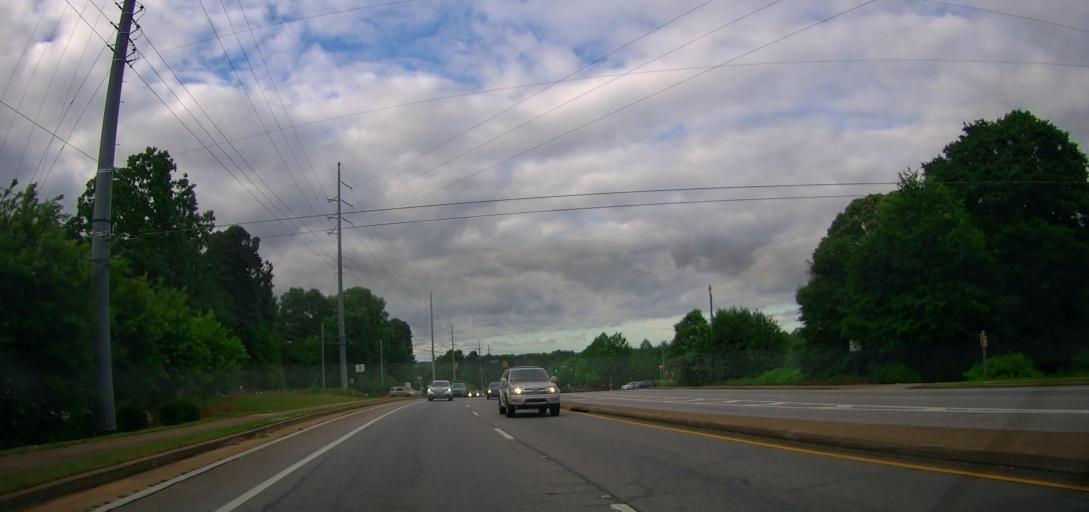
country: US
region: Georgia
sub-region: Clarke County
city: Country Club Estates
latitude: 33.9327
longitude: -83.4379
